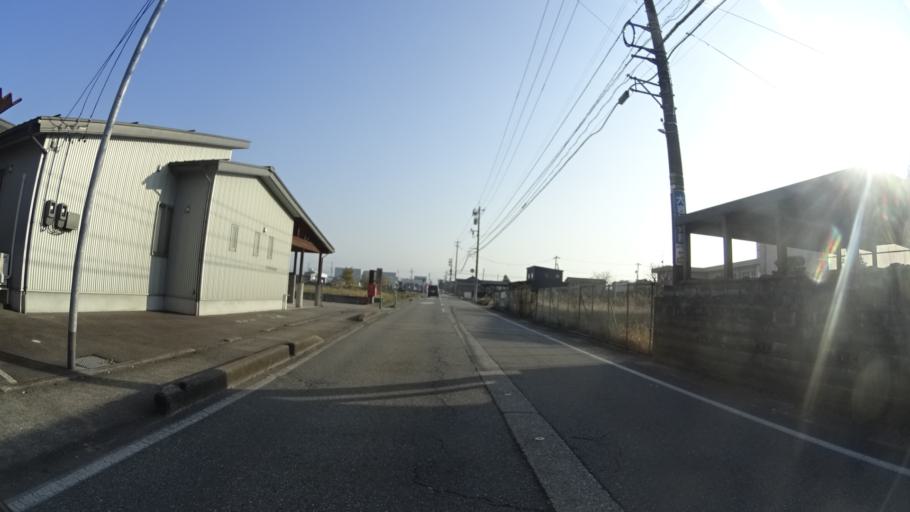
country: JP
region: Toyama
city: Toyama-shi
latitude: 36.6939
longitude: 137.2688
